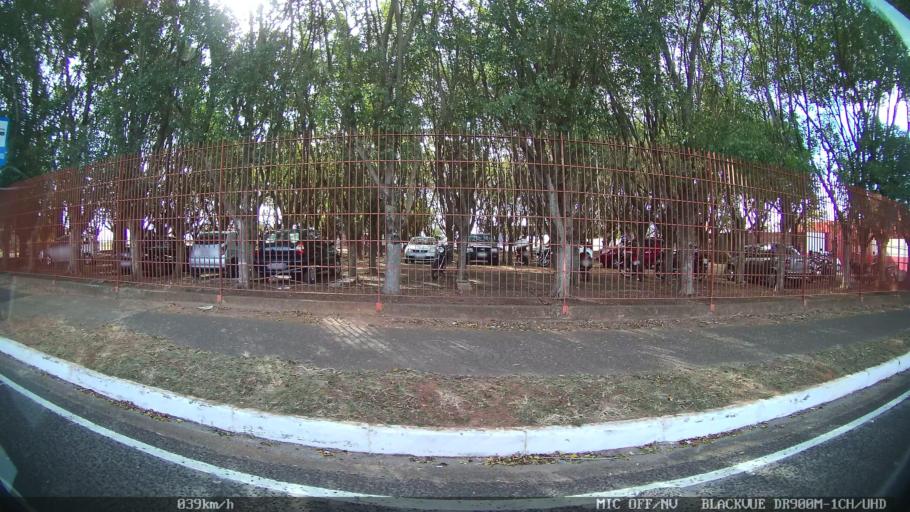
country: BR
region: Sao Paulo
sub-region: Sao Jose Do Rio Preto
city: Sao Jose do Rio Preto
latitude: -20.8008
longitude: -49.3448
